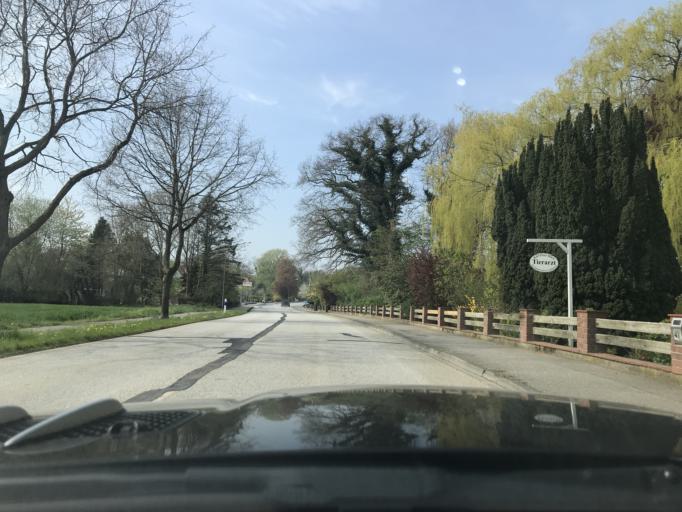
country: DE
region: Schleswig-Holstein
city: Riepsdorf
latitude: 54.1940
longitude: 10.9898
